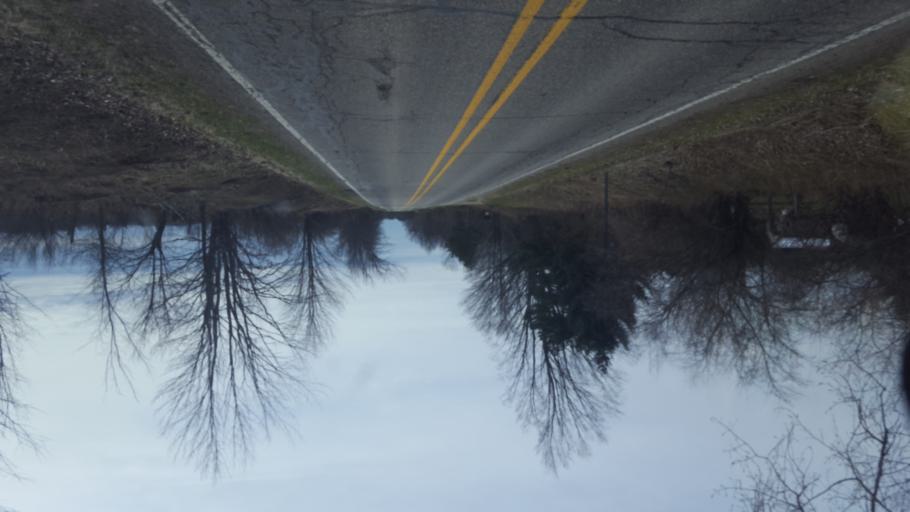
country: US
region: Michigan
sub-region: Isabella County
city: Lake Isabella
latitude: 43.5660
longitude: -85.0262
